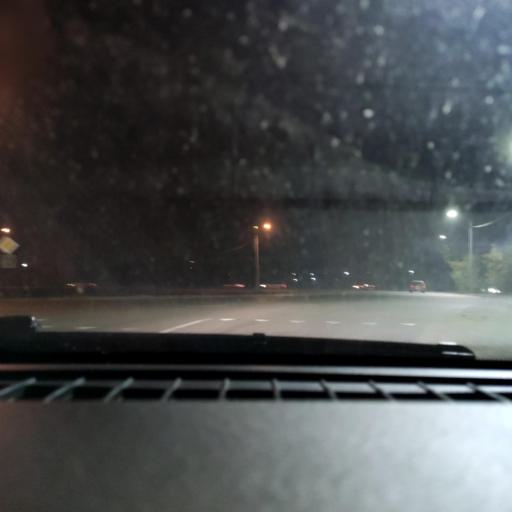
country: RU
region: Voronezj
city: Maslovka
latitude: 51.6224
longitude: 39.2622
